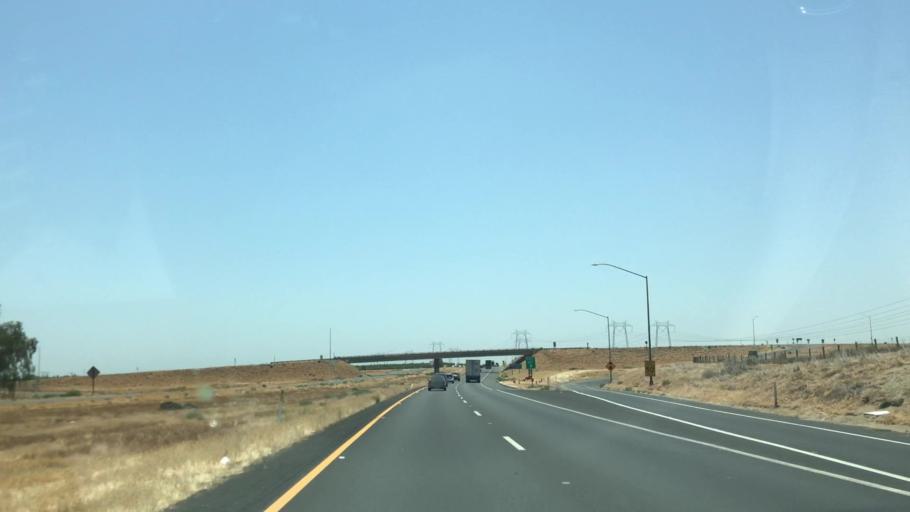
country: US
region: California
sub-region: Fresno County
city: Coalinga
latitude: 36.2969
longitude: -120.2711
